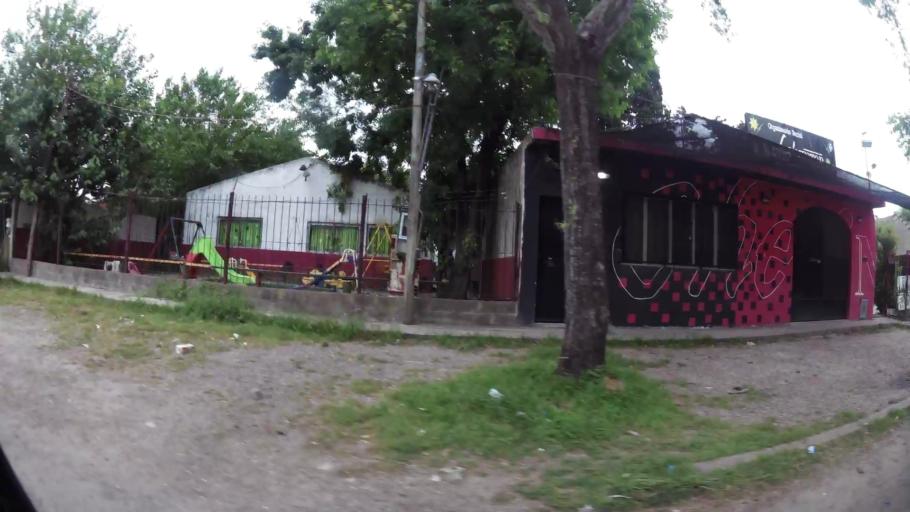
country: AR
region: Buenos Aires
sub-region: Partido de La Plata
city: La Plata
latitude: -34.9383
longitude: -57.9924
